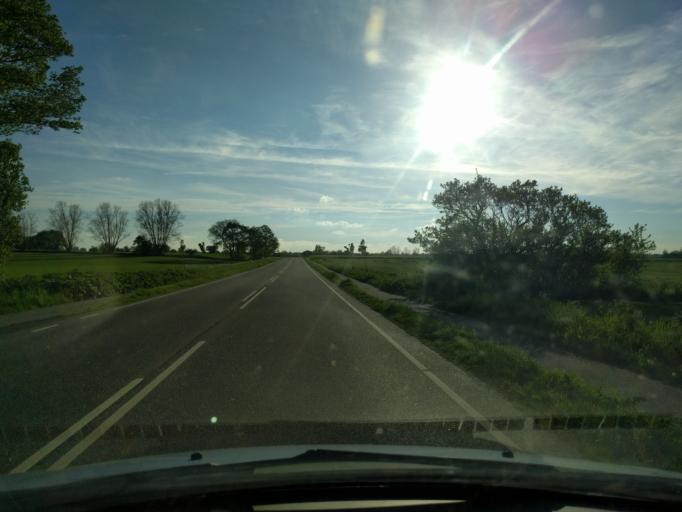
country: DK
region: Zealand
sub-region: Guldborgsund Kommune
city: Stubbekobing
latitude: 54.7974
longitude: 11.9887
